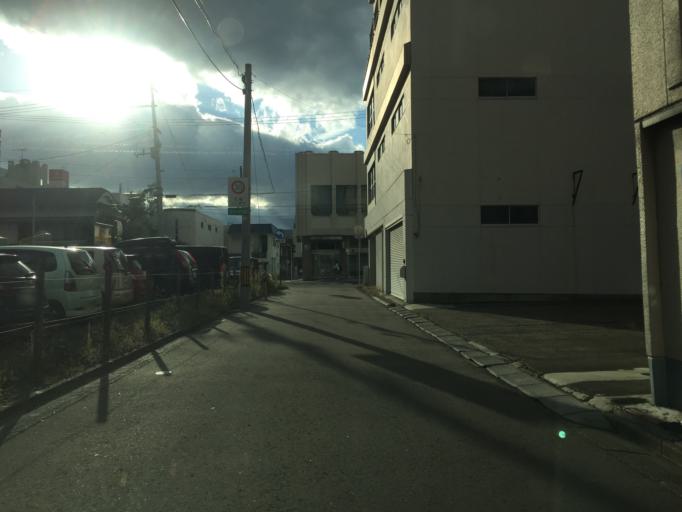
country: JP
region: Fukushima
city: Fukushima-shi
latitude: 37.7522
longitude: 140.4653
